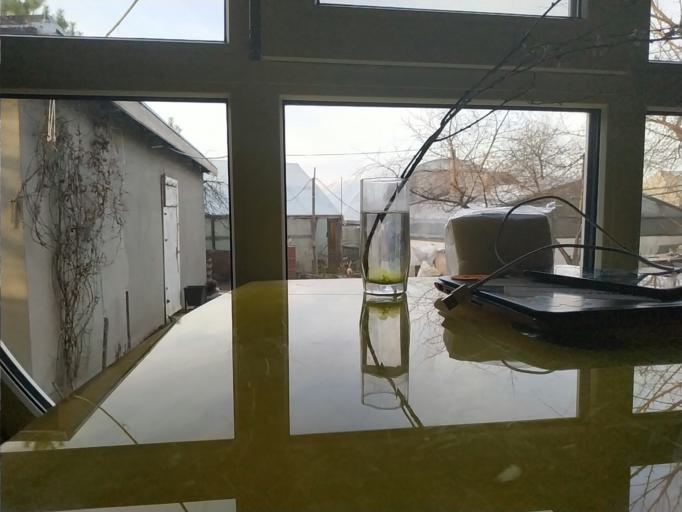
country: RU
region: Republic of Karelia
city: Suoyarvi
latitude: 62.1607
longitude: 32.1362
